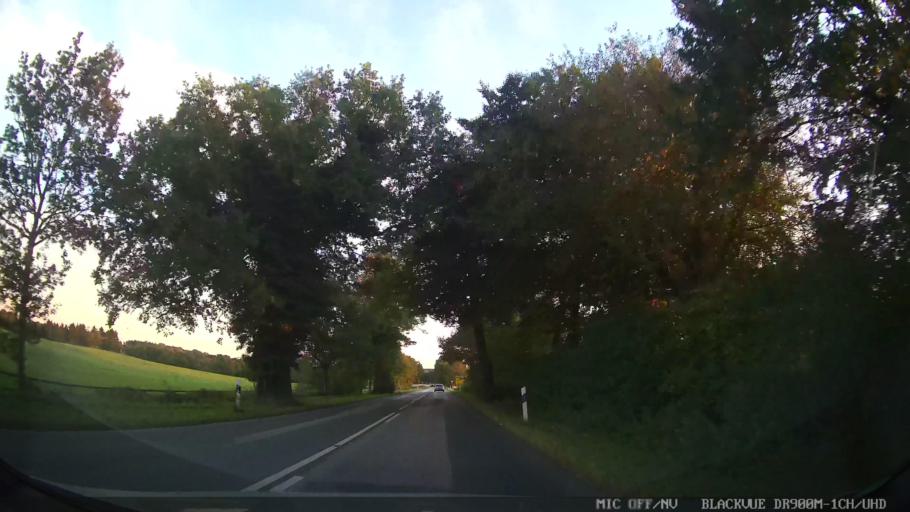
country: DE
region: Schleswig-Holstein
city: Susel
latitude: 54.0166
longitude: 10.6866
